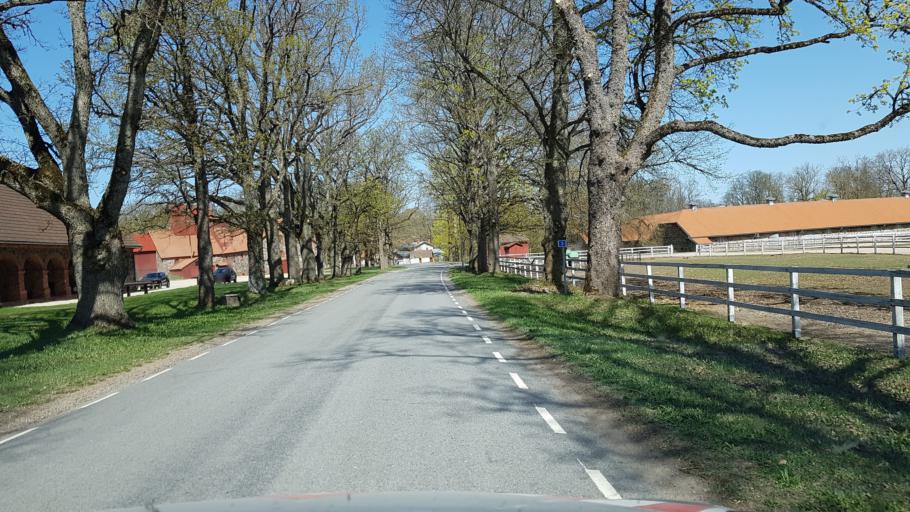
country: EE
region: Viljandimaa
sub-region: Vohma linn
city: Vohma
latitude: 58.5513
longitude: 25.5653
